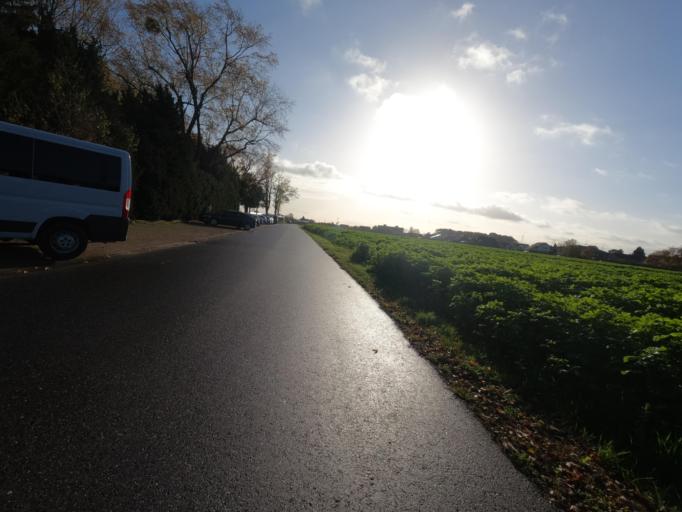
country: DE
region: North Rhine-Westphalia
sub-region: Regierungsbezirk Koln
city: Wassenberg
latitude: 51.0594
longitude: 6.1585
